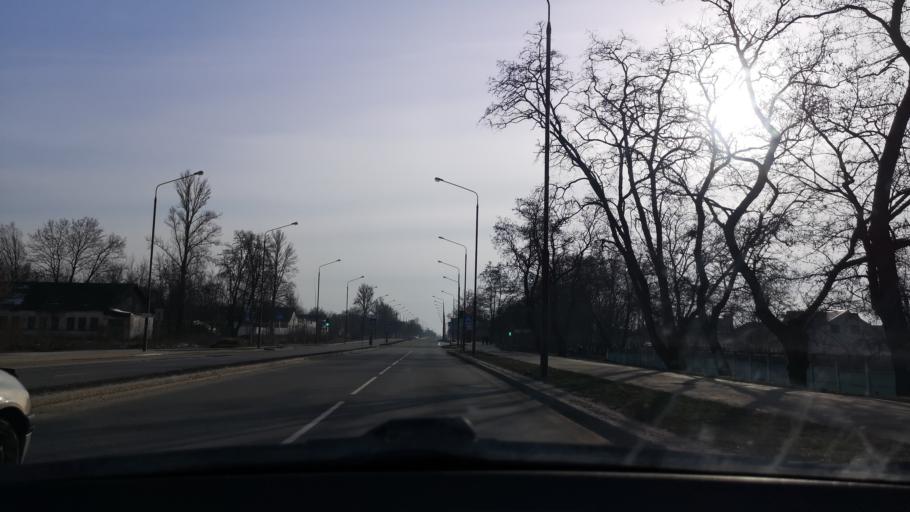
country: BY
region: Brest
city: Brest
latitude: 52.1302
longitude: 23.6738
